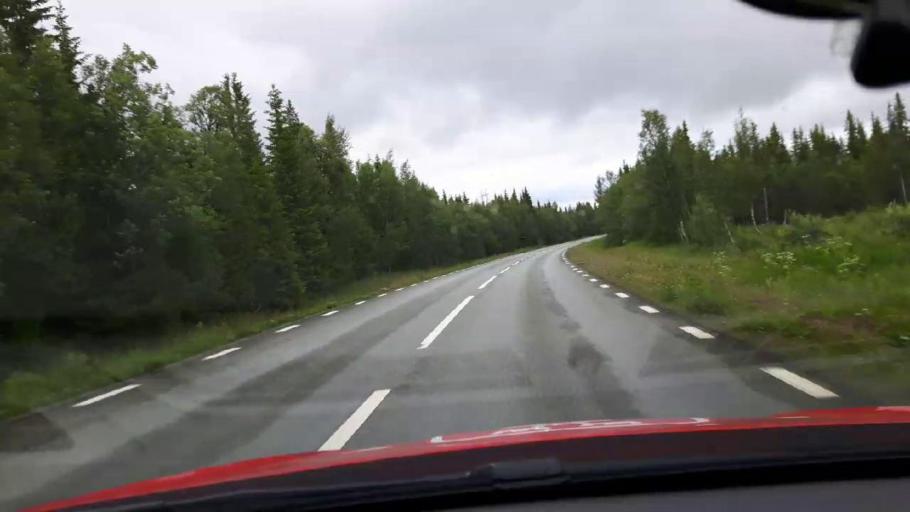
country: SE
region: Jaemtland
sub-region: Are Kommun
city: Are
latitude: 63.3321
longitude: 12.5581
